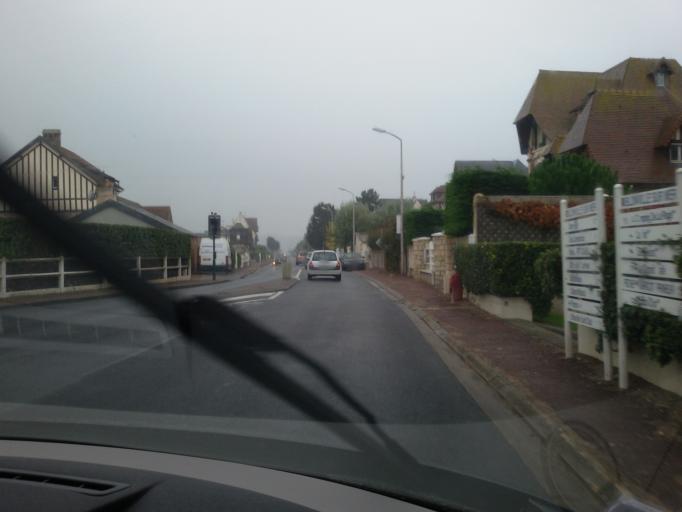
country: FR
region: Lower Normandy
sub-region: Departement du Calvados
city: Blonville-sur-Mer
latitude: 49.3379
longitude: 0.0256
